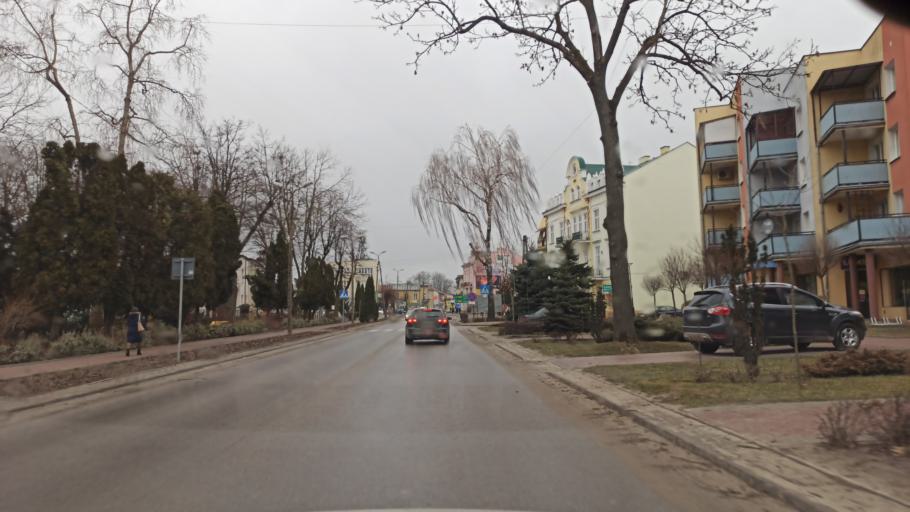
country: PL
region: Lublin Voivodeship
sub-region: Powiat lubelski
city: Bychawa
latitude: 51.0141
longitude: 22.5370
